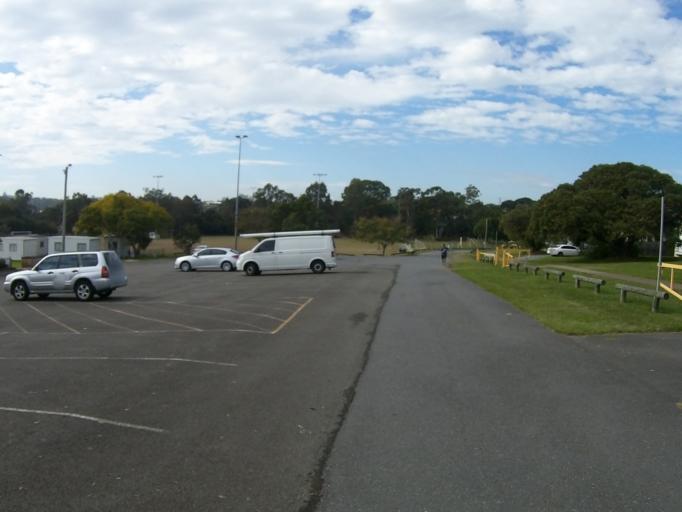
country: AU
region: Queensland
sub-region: Brisbane
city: Greenslopes
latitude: -27.5185
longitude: 153.0477
